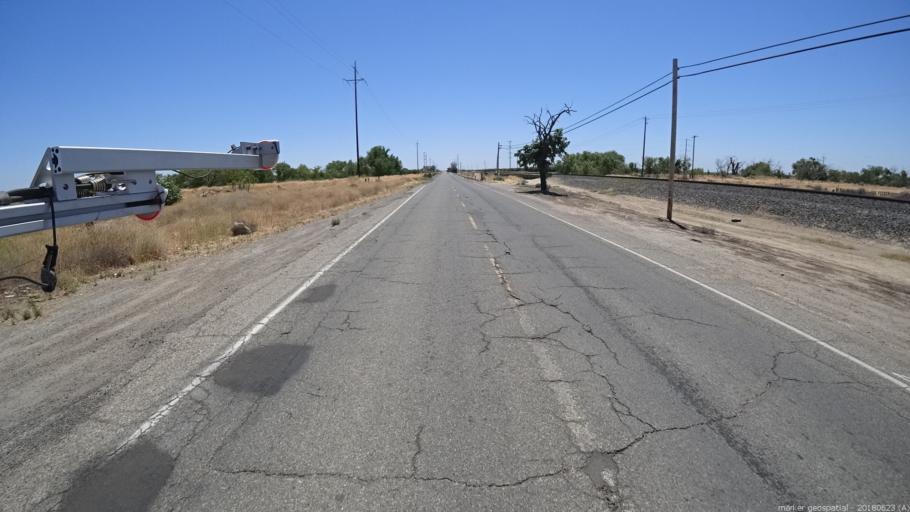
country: US
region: California
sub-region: Madera County
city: Chowchilla
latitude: 37.1073
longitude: -120.2353
